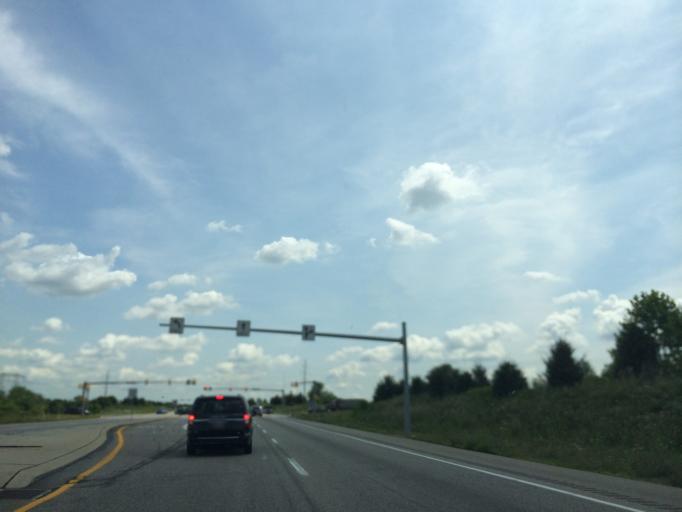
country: US
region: Pennsylvania
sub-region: Lehigh County
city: Wescosville
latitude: 40.5654
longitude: -75.5661
